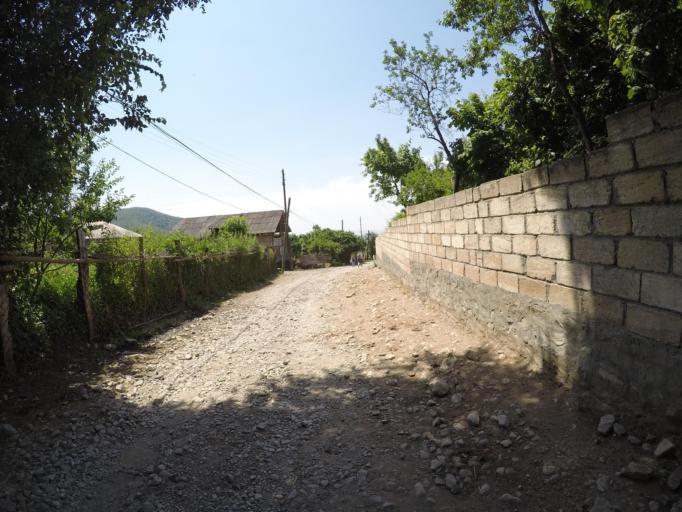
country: AZ
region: Qakh Rayon
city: Cinarli
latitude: 41.4835
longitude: 46.8493
